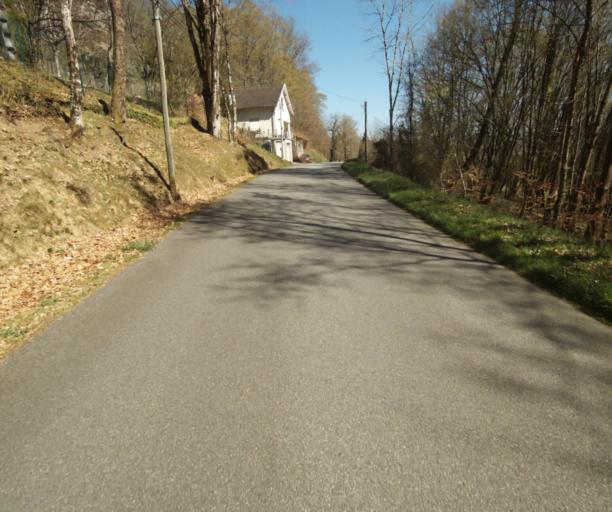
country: FR
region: Limousin
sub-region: Departement de la Correze
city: Tulle
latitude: 45.2593
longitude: 1.7347
